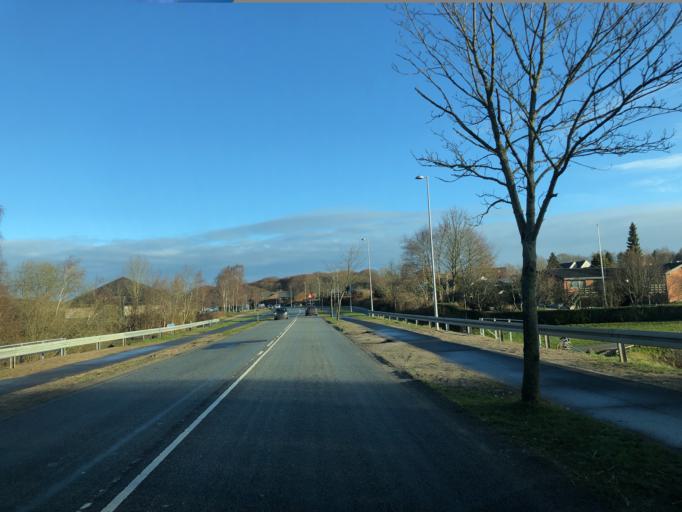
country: DK
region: Central Jutland
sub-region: Favrskov Kommune
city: Hinnerup
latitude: 56.2576
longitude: 10.0708
